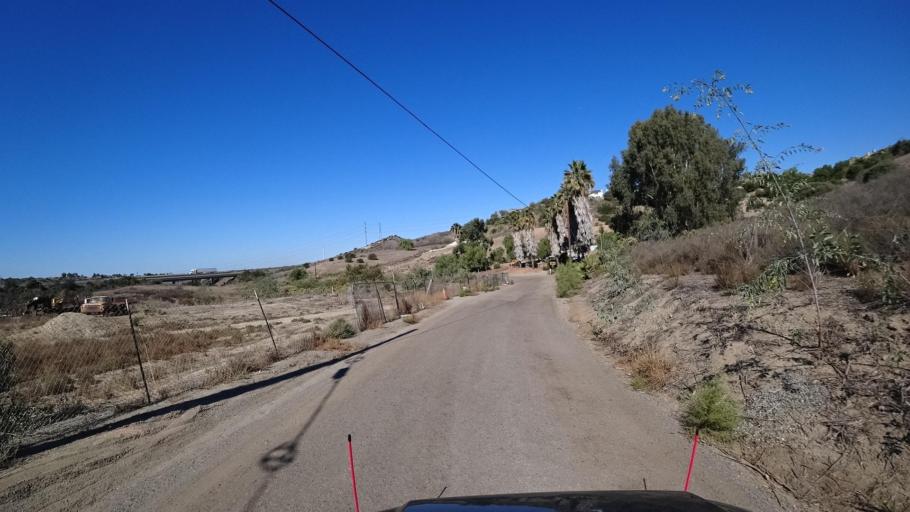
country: US
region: California
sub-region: San Diego County
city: La Presa
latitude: 32.6654
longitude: -116.9806
